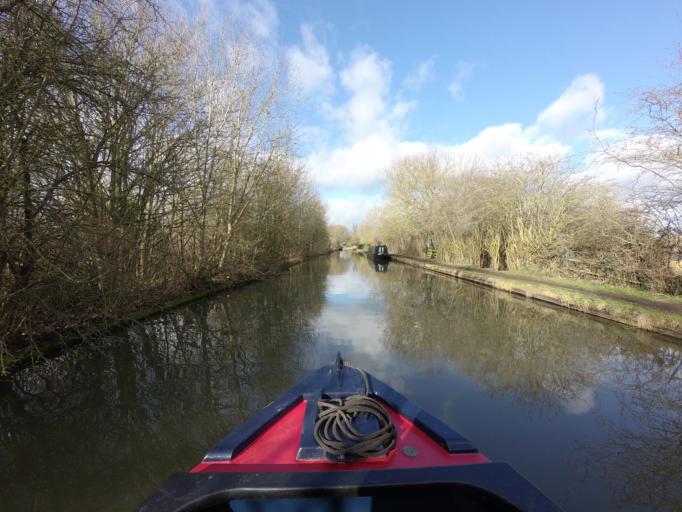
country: GB
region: England
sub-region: Northamptonshire
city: Bugbrooke
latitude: 52.2303
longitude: -1.0754
